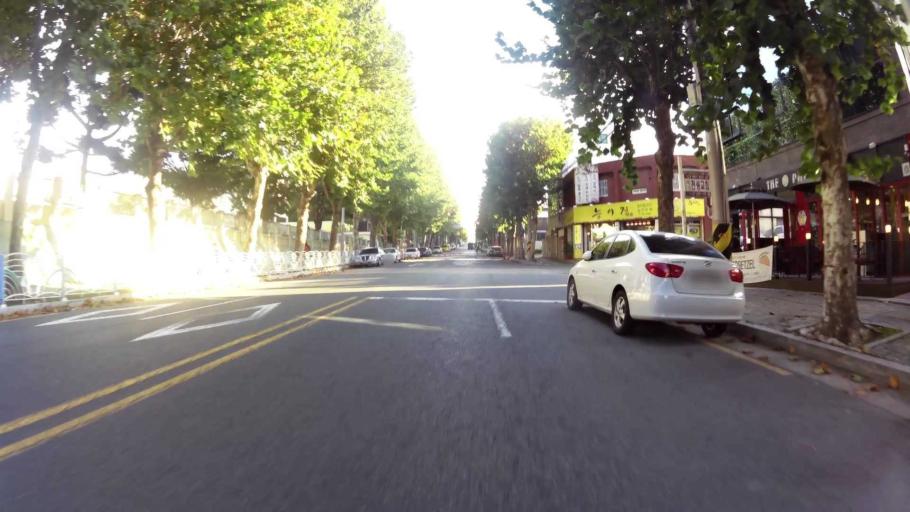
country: KR
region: Daegu
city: Daegu
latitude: 35.8653
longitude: 128.6390
